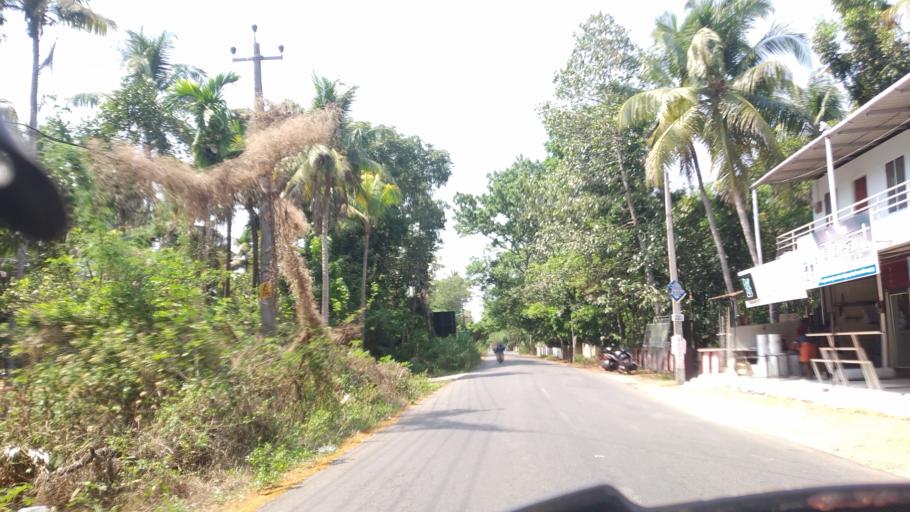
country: IN
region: Kerala
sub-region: Thrissur District
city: Kodungallur
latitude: 10.2411
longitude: 76.1513
